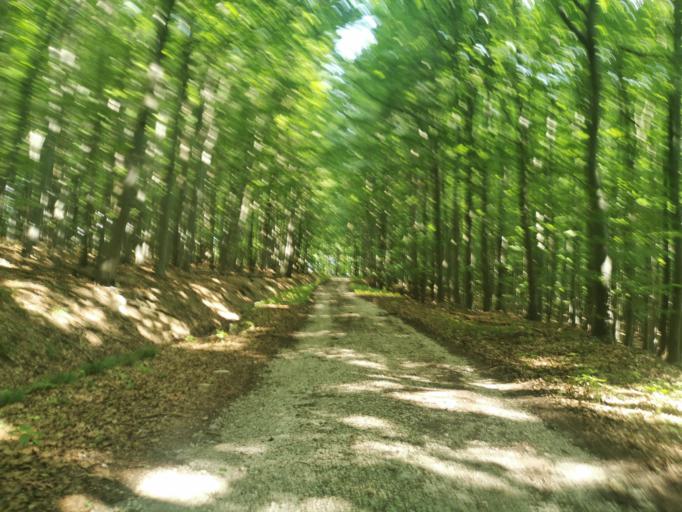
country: SK
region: Trenciansky
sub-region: Okres Myjava
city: Myjava
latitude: 48.8144
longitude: 17.5703
